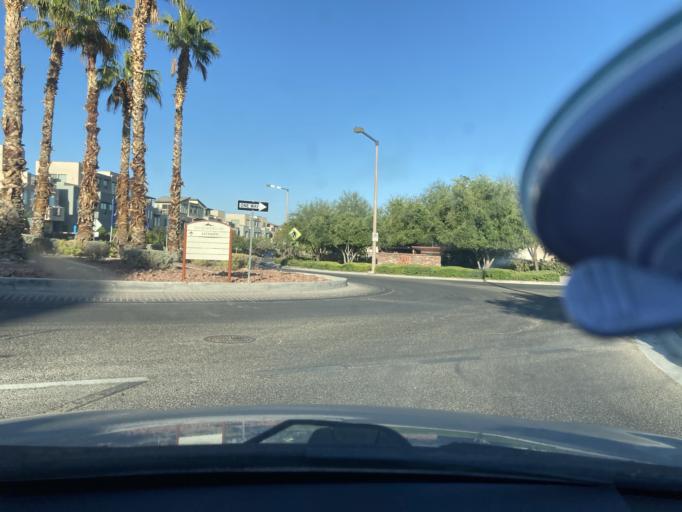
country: US
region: Nevada
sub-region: Clark County
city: Summerlin South
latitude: 36.1563
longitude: -115.3444
